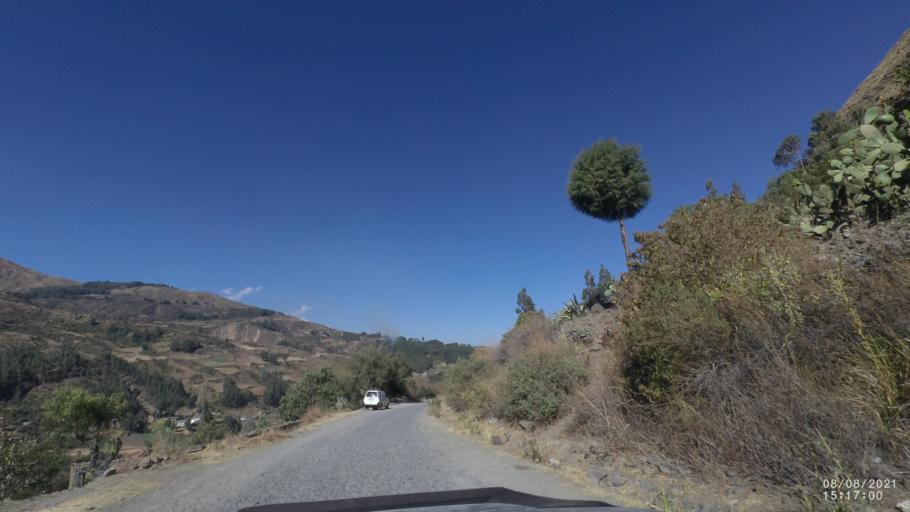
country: BO
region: Cochabamba
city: Cochabamba
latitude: -17.2856
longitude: -66.3056
